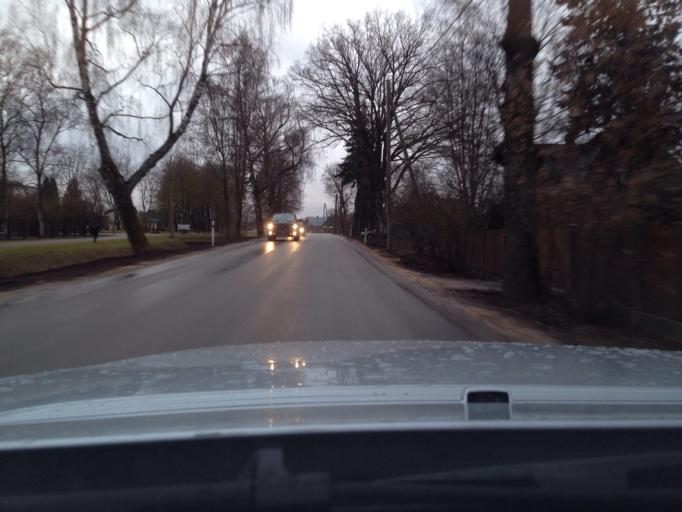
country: LV
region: Marupe
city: Marupe
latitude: 56.8996
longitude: 24.0469
